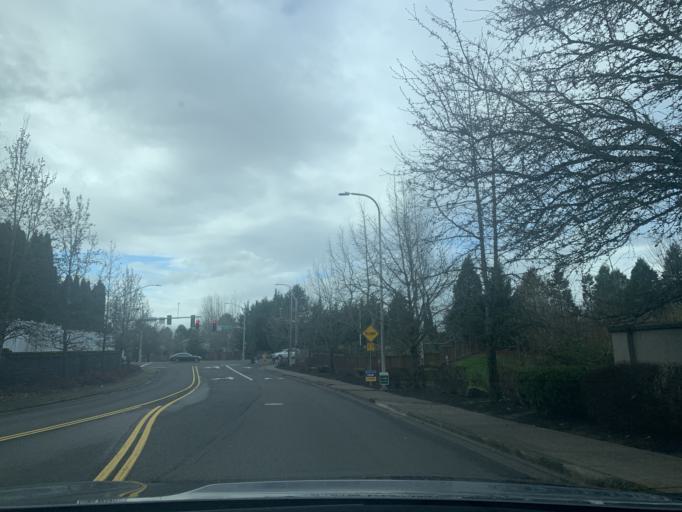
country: US
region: Oregon
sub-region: Washington County
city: Oak Hills
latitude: 45.5598
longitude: -122.8332
